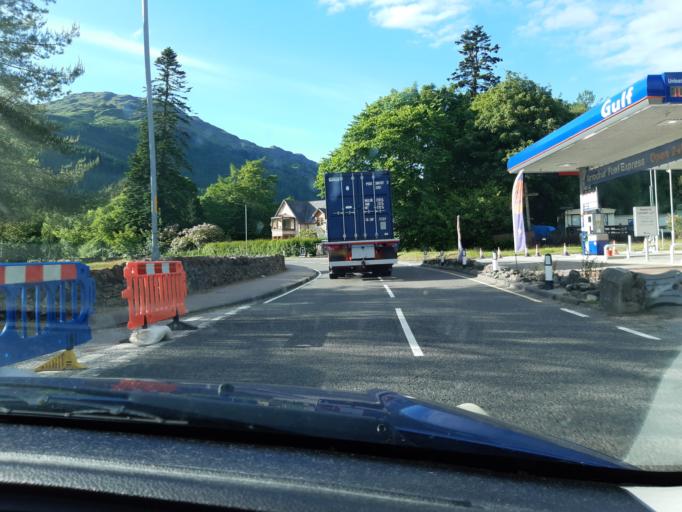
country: GB
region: Scotland
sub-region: Argyll and Bute
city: Garelochhead
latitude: 56.2060
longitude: -4.7443
